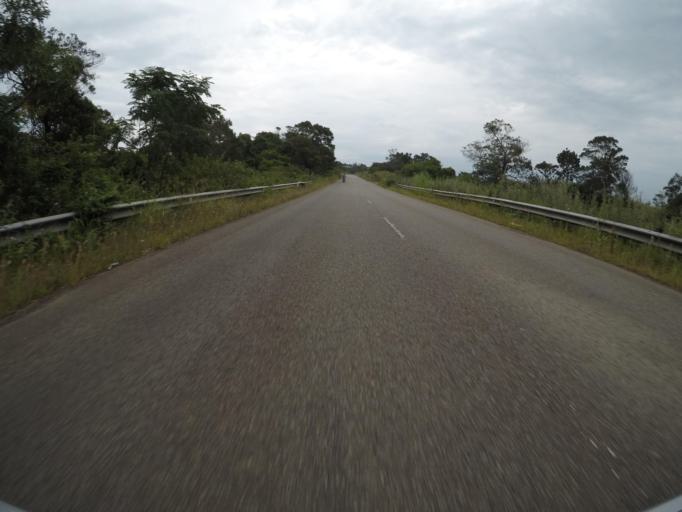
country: ZA
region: Eastern Cape
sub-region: Buffalo City Metropolitan Municipality
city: East London
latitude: -32.9666
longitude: 27.9035
